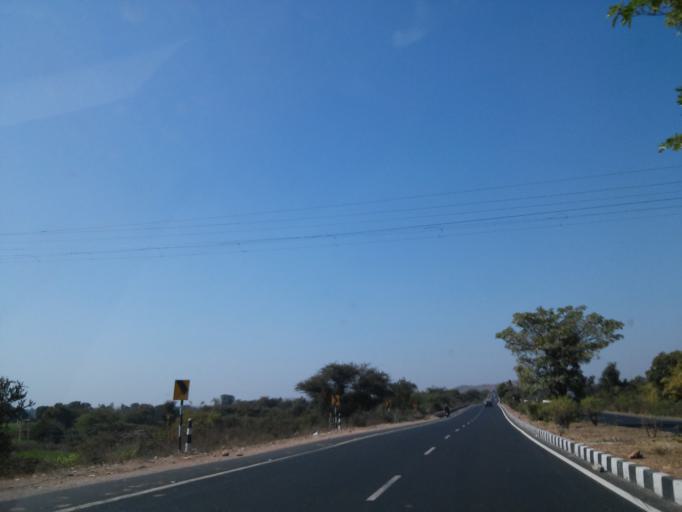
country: IN
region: Gujarat
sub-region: Sabar Kantha
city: Modasa
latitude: 23.5986
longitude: 73.2007
